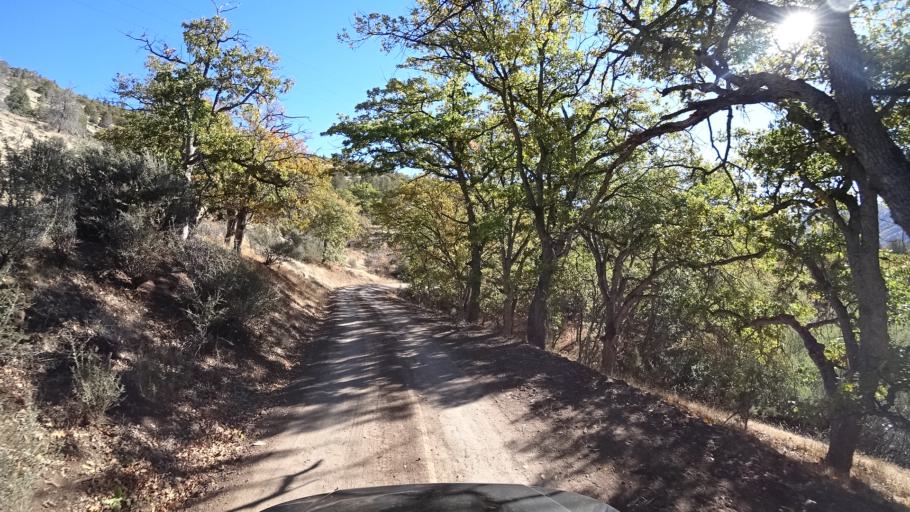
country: US
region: California
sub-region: Siskiyou County
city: Montague
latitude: 41.9808
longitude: -122.2929
